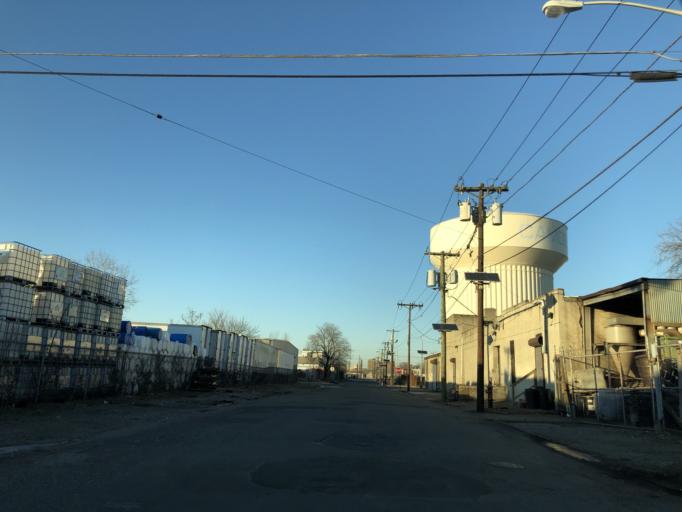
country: US
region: New Jersey
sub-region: Camden County
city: Camden
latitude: 39.9296
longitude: -75.1255
